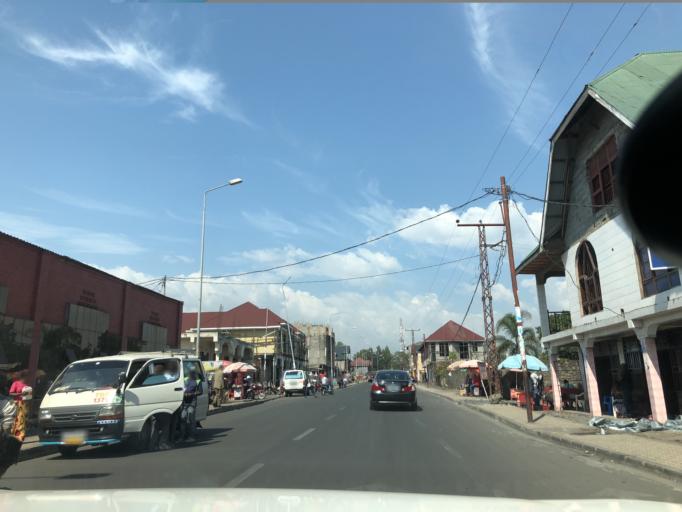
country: CD
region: Nord Kivu
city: Goma
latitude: -1.6608
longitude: 29.1868
